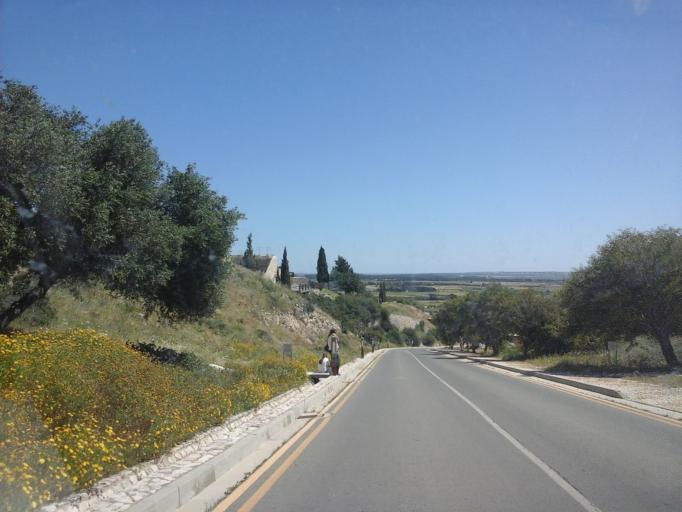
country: CY
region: Limassol
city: Erimi
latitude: 34.6647
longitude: 32.8864
